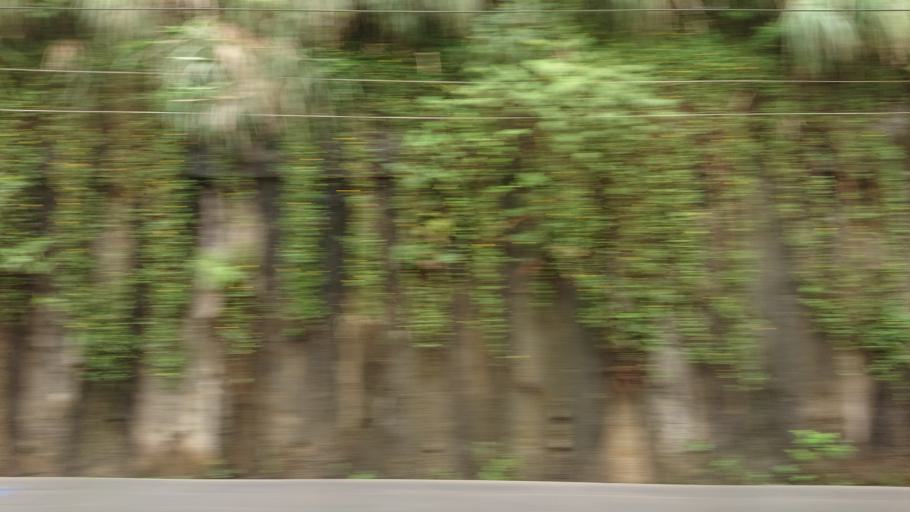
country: TW
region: Taiwan
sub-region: Keelung
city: Keelung
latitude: 25.0783
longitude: 121.6954
